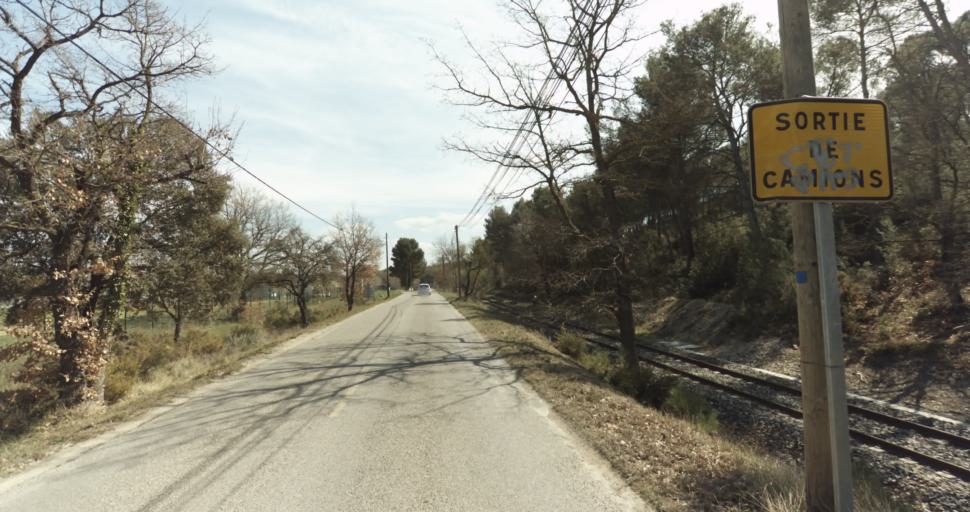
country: FR
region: Provence-Alpes-Cote d'Azur
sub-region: Departement des Bouches-du-Rhone
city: Ventabren
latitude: 43.5063
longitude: 5.3344
